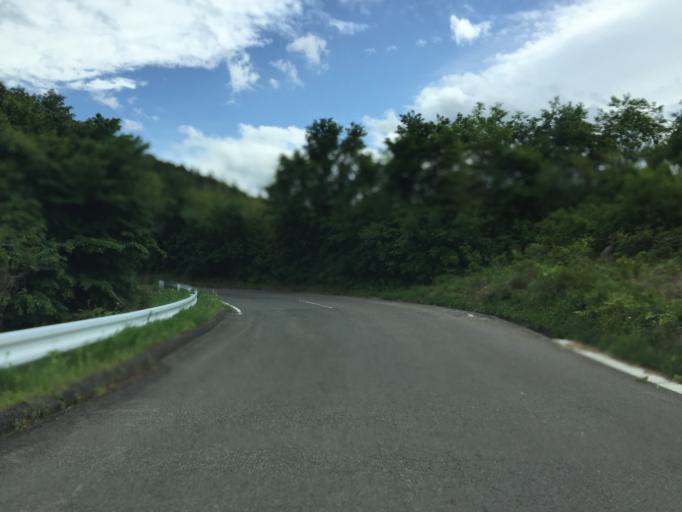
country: JP
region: Fukushima
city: Nihommatsu
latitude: 37.6336
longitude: 140.5053
